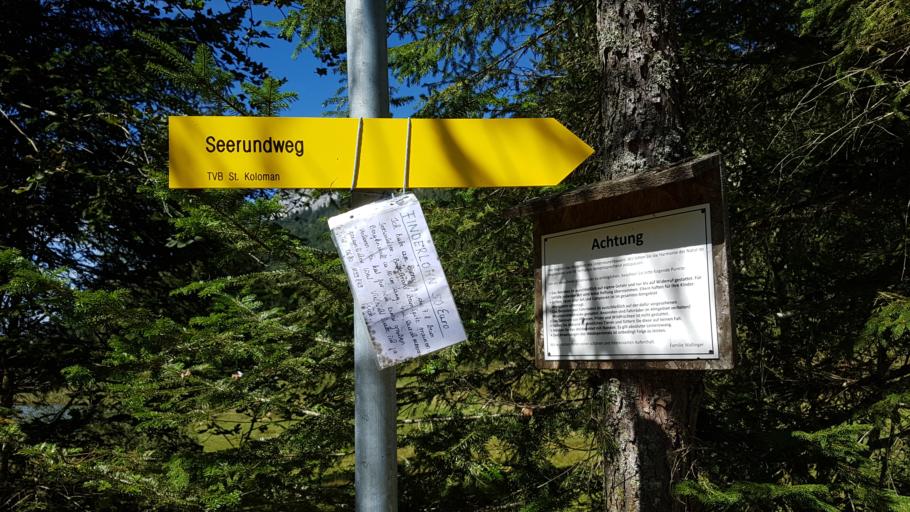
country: AT
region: Salzburg
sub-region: Politischer Bezirk Hallein
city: Scheffau am Tennengebirge
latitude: 47.6272
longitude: 13.2784
